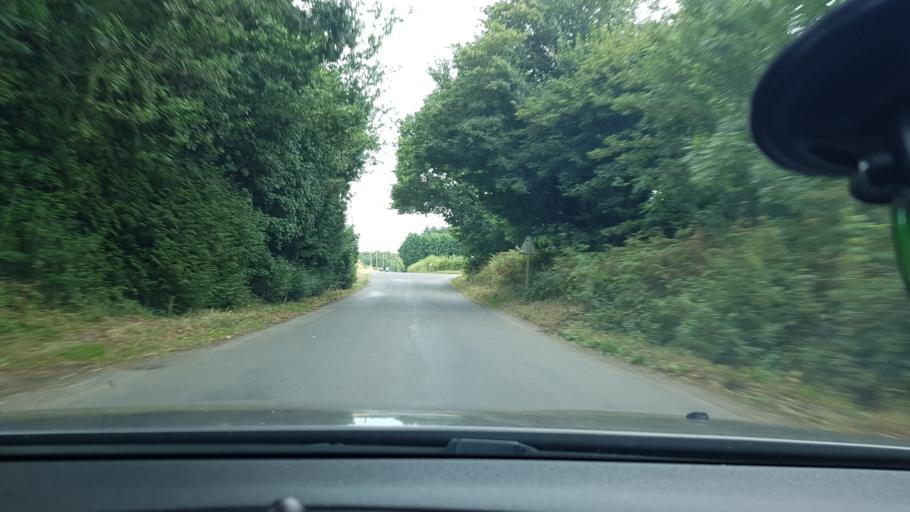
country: GB
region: England
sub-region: West Berkshire
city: Lambourn
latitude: 51.4743
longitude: -1.5522
